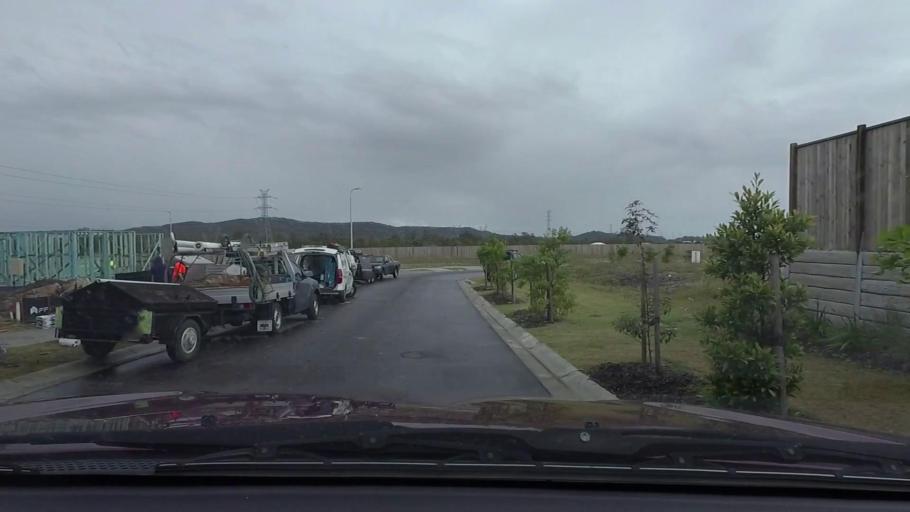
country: AU
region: Queensland
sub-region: Logan
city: Chambers Flat
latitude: -27.8182
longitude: 153.1308
